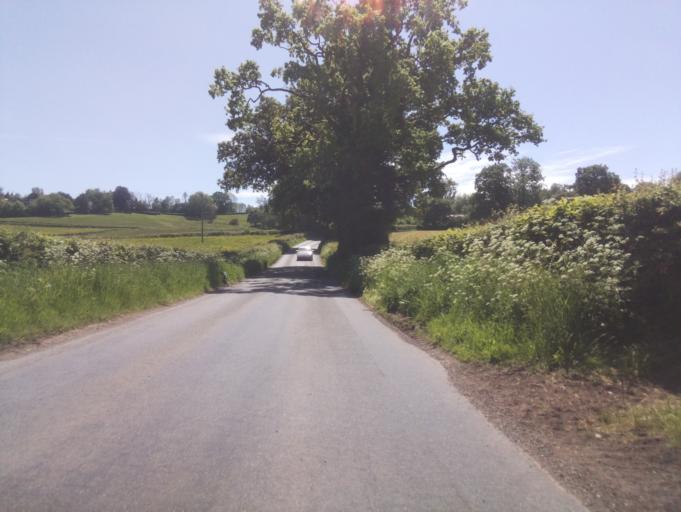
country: GB
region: Wales
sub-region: Monmouthshire
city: Caldicot
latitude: 51.6469
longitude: -2.7559
